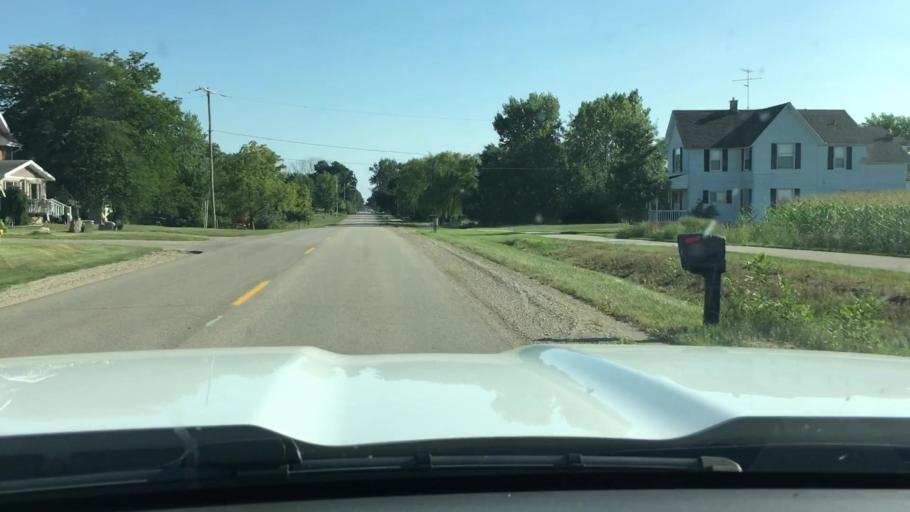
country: US
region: Michigan
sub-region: Ottawa County
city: Zeeland
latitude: 42.7878
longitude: -85.9404
